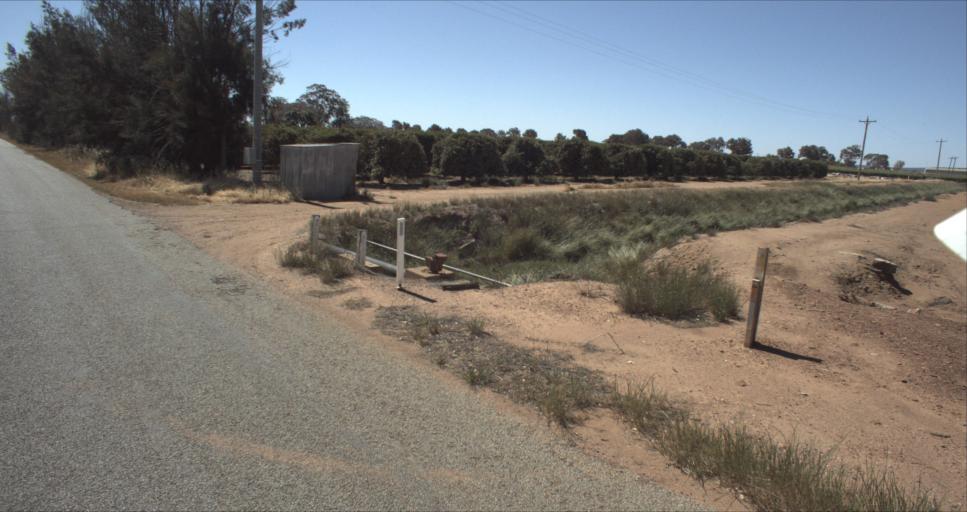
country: AU
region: New South Wales
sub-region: Leeton
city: Leeton
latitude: -34.5365
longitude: 146.3582
